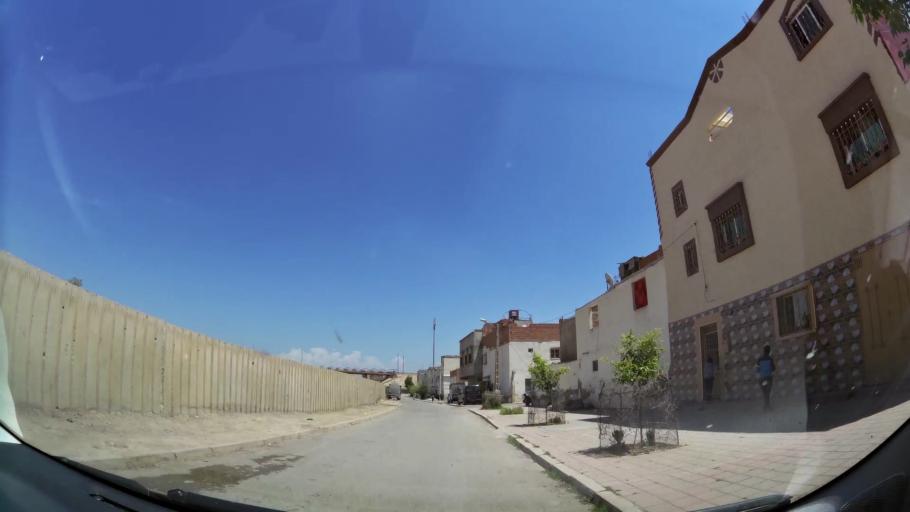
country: MA
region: Oriental
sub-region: Oujda-Angad
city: Oujda
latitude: 34.6940
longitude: -1.9444
